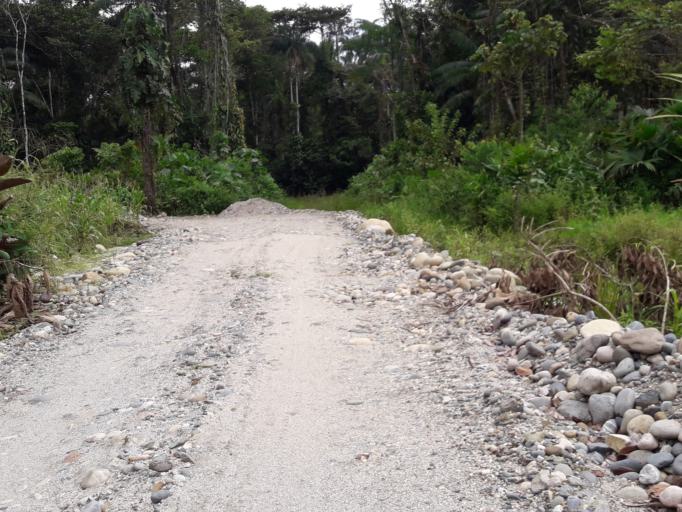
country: EC
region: Napo
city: Tena
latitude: -1.0546
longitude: -77.7926
